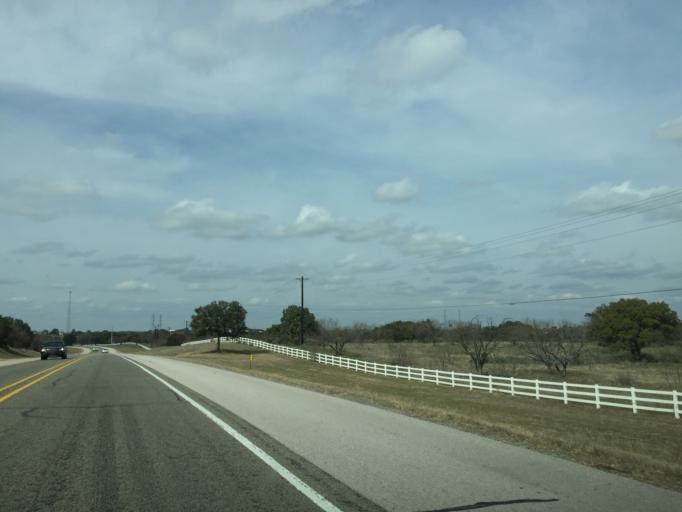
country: US
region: Texas
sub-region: Burnet County
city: Granite Shoals
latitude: 30.5234
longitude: -98.4159
